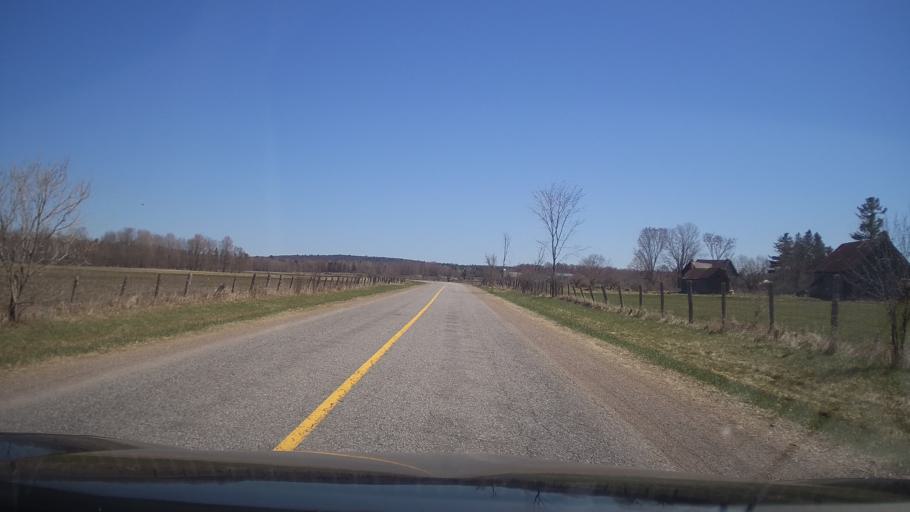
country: CA
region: Quebec
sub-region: Outaouais
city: Shawville
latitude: 45.5463
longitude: -76.3878
